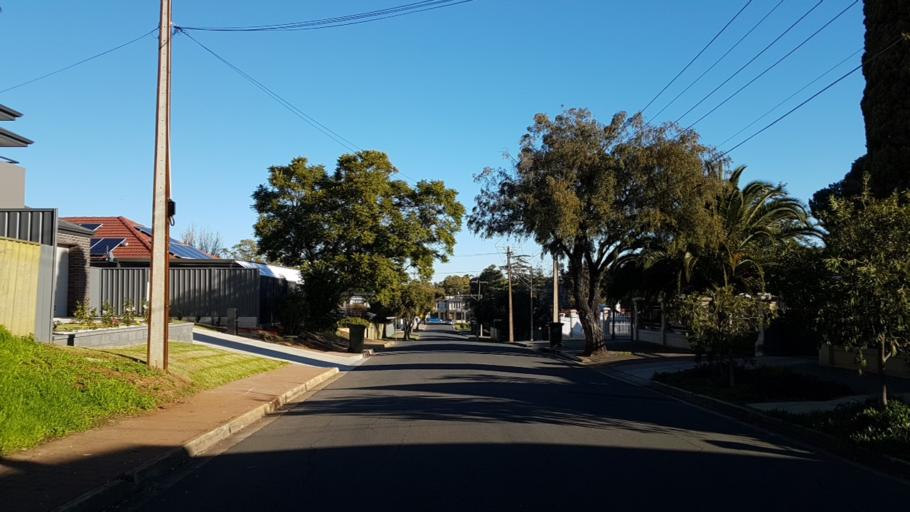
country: AU
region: South Australia
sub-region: Campbelltown
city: Campbelltown
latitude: -34.8811
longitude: 138.6591
